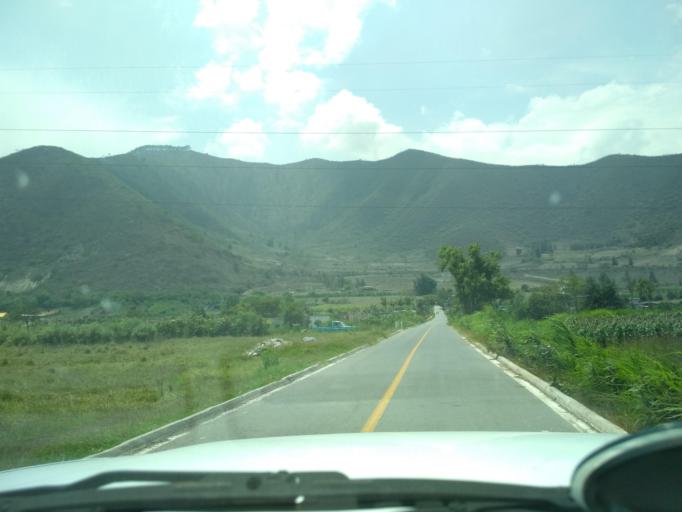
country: MX
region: Veracruz
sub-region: Nogales
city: Taza de Agua Ojo Zarco
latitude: 18.7756
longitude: -97.2184
